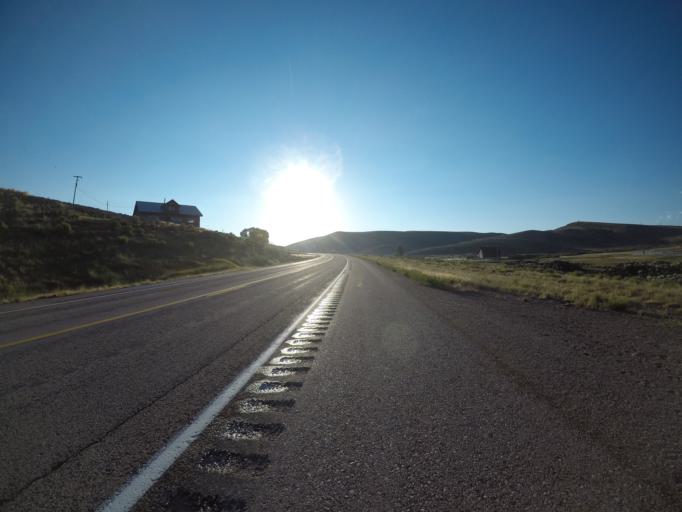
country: US
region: Wyoming
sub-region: Lincoln County
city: Kemmerer
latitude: 41.8698
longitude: -110.4985
